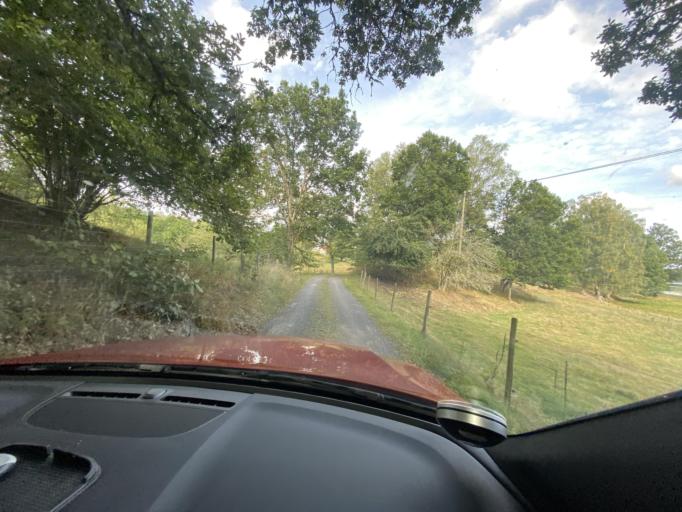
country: SE
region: Skane
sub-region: Hassleholms Kommun
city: Hastveda
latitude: 56.3577
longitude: 13.8795
